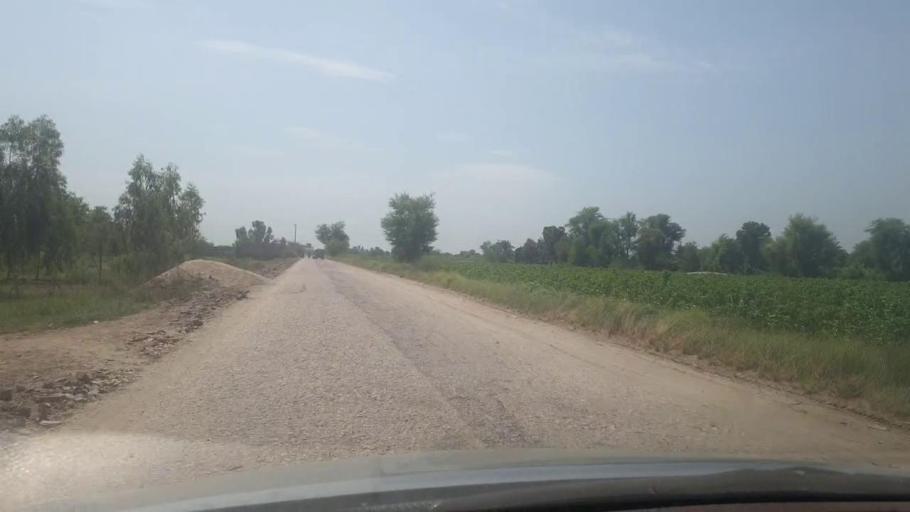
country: PK
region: Sindh
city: Bozdar
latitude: 27.2189
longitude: 68.5685
